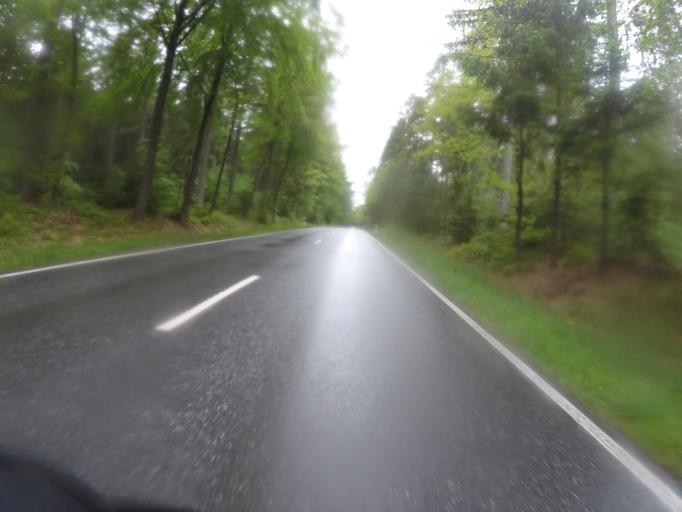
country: DE
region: Schleswig-Holstein
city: Heidmuhlen
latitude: 53.9454
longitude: 10.0862
